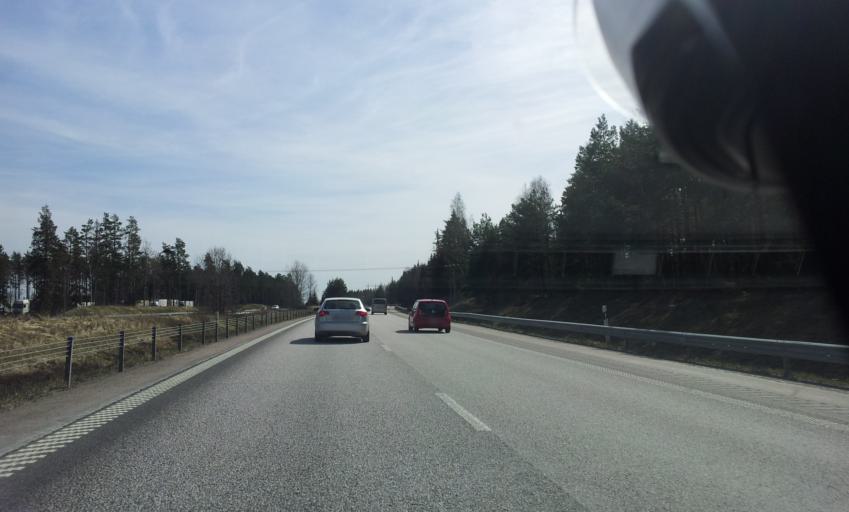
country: SE
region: Uppsala
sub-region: Uppsala Kommun
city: Alsike
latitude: 59.7963
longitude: 17.7720
